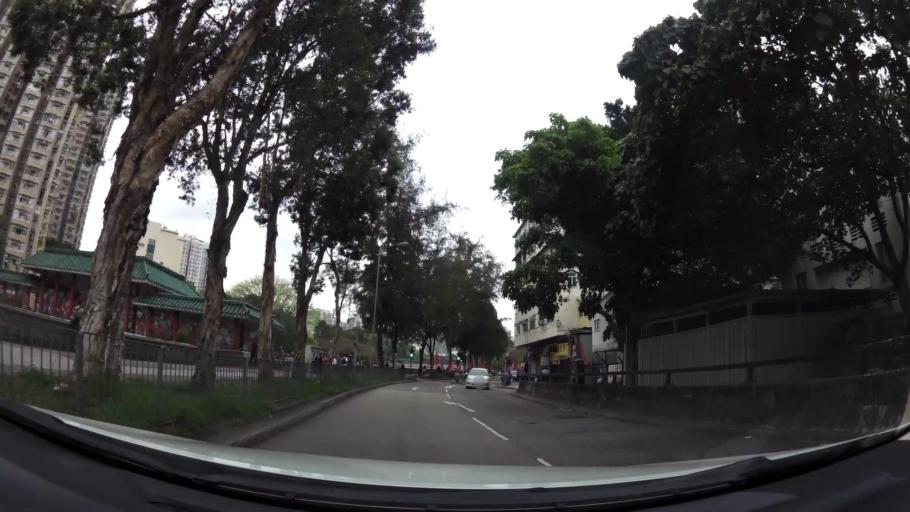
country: HK
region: Tai Po
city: Tai Po
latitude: 22.4495
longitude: 114.1628
